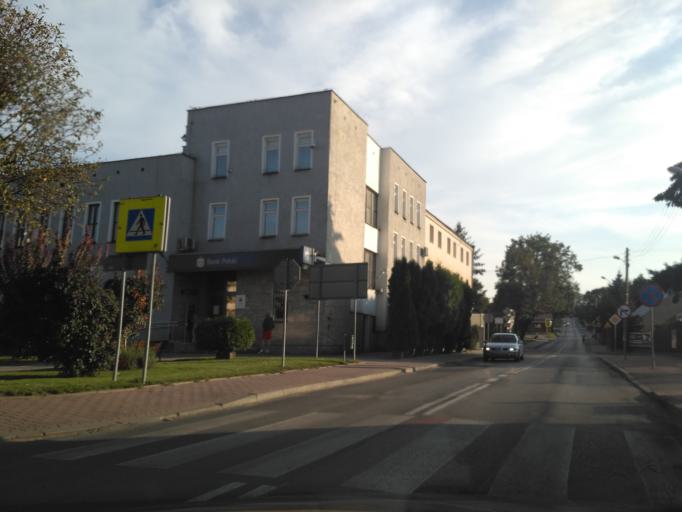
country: PL
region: Lublin Voivodeship
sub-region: Powiat lubelski
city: Bychawa
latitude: 51.0148
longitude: 22.5350
